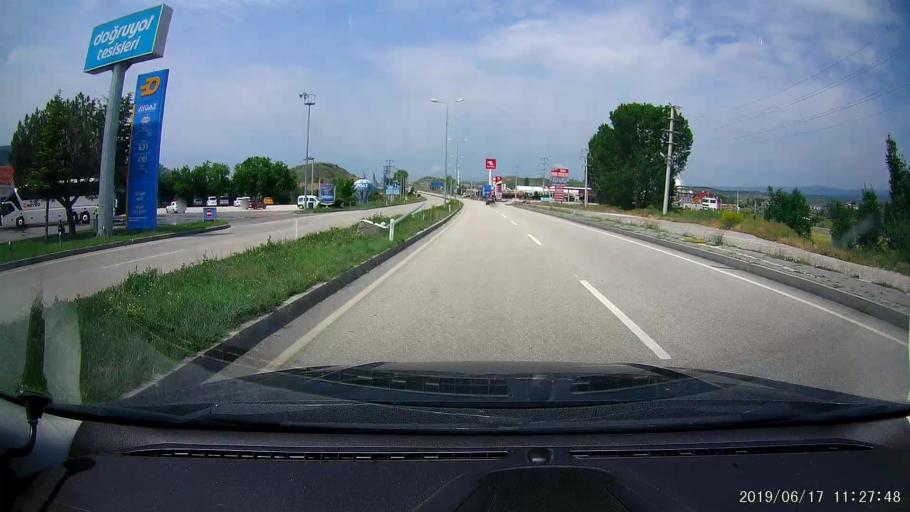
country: TR
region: Cankiri
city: Ilgaz
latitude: 40.9087
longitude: 33.6322
